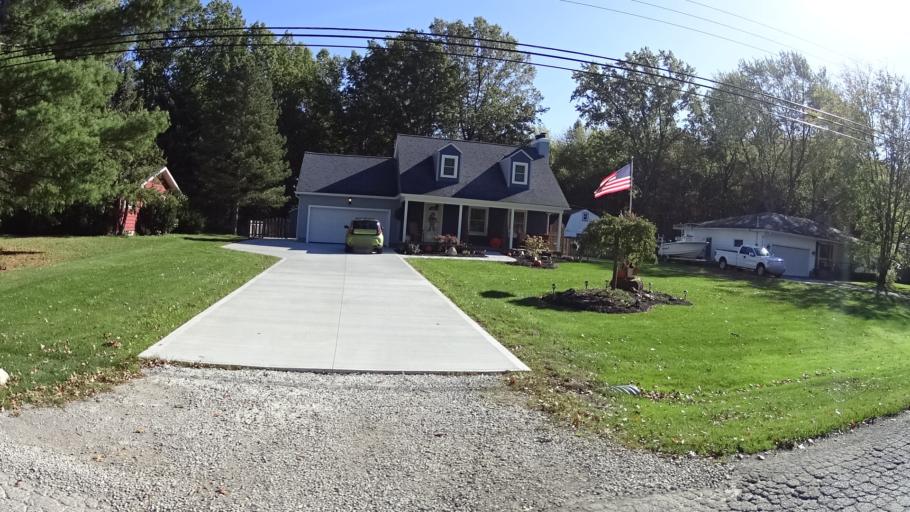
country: US
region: Ohio
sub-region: Lorain County
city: Lorain
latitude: 41.4163
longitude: -82.1701
